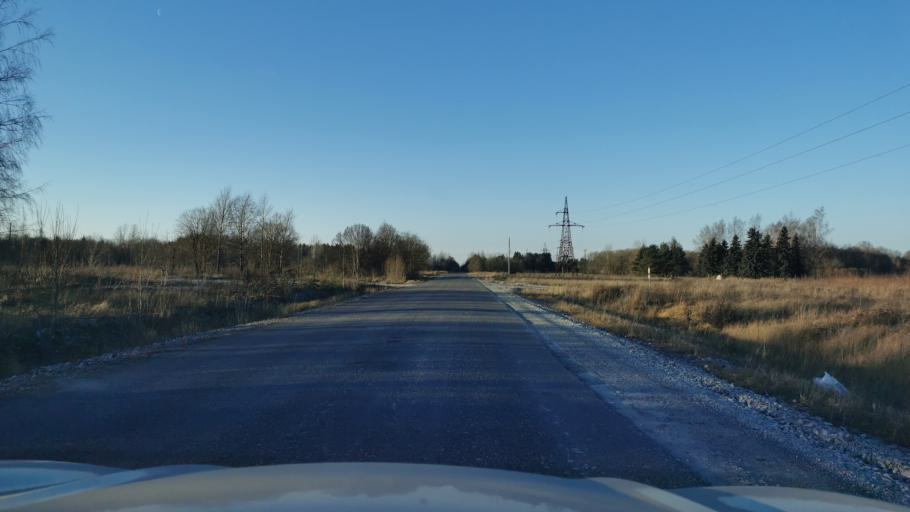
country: EE
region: Ida-Virumaa
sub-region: Puessi linn
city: Pussi
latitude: 59.3405
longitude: 27.0724
